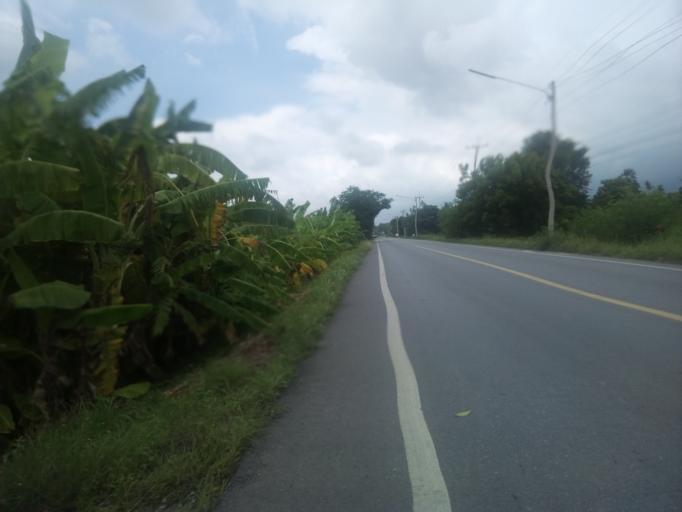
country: TH
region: Pathum Thani
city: Ban Lam Luk Ka
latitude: 13.9815
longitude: 100.8203
